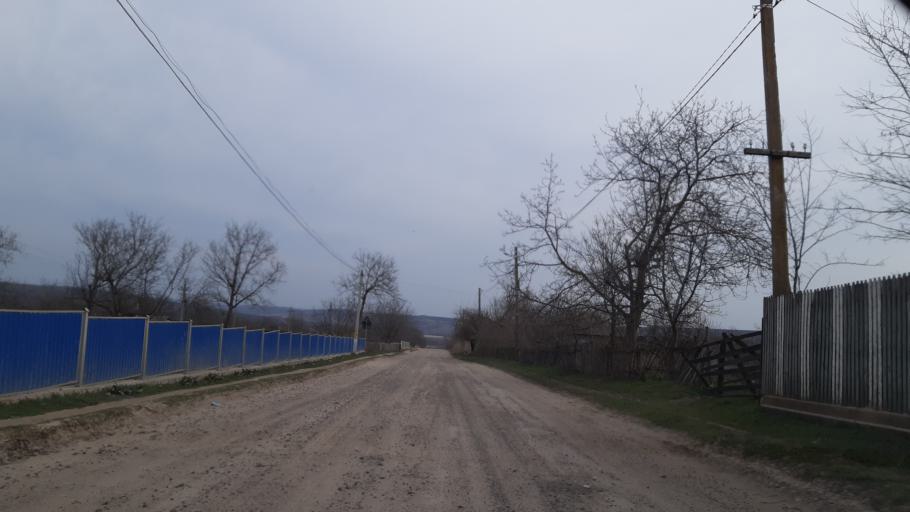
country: MD
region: Soldanesti
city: Soldanesti
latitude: 47.7114
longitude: 28.7068
